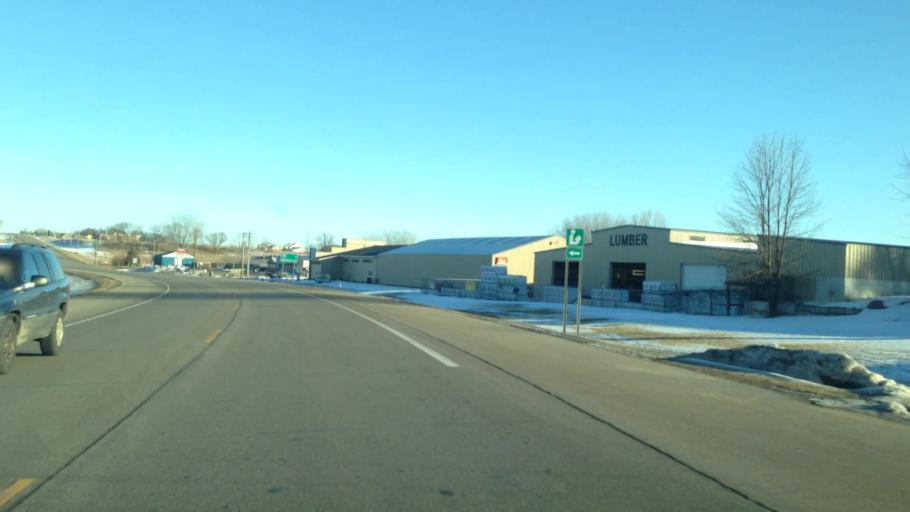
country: US
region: Minnesota
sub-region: Rice County
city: Lonsdale
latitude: 44.4793
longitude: -93.4205
